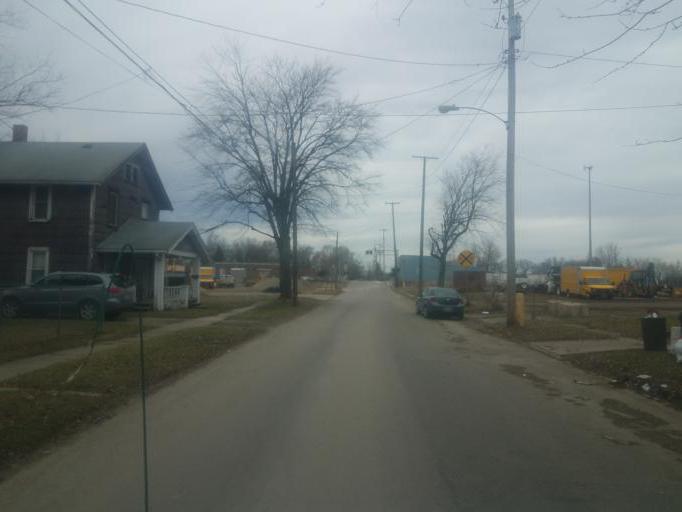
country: US
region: Ohio
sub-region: Marion County
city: Marion
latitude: 40.5935
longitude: -83.1067
